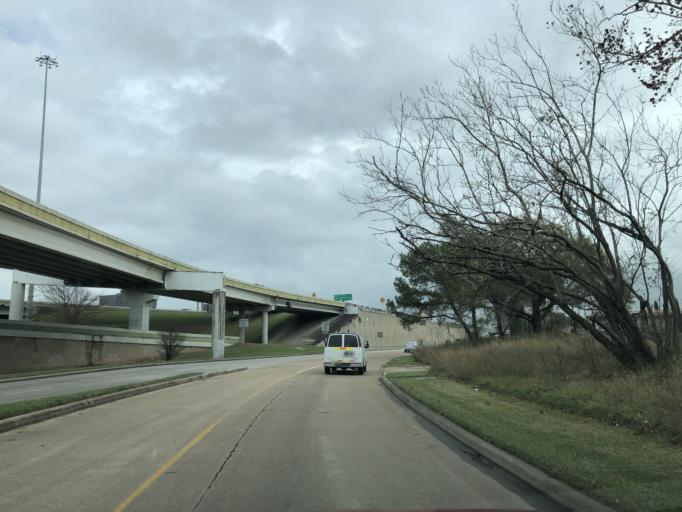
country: US
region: Texas
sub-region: Harris County
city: Aldine
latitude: 29.9396
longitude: -95.4119
